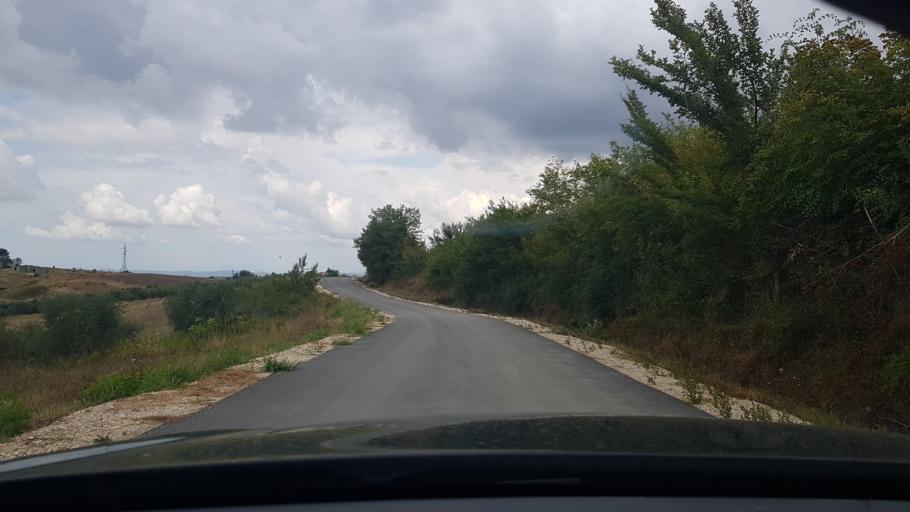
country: AL
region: Durres
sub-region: Rrethi i Durresit
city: Gjepalaj
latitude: 41.3038
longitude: 19.5532
